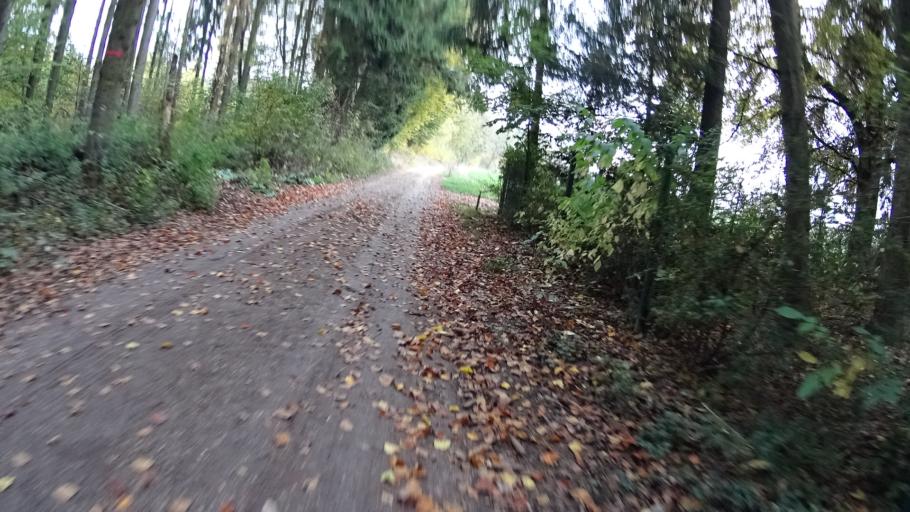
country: DE
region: Bavaria
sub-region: Upper Bavaria
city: Hitzhofen
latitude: 48.8620
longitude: 11.3036
